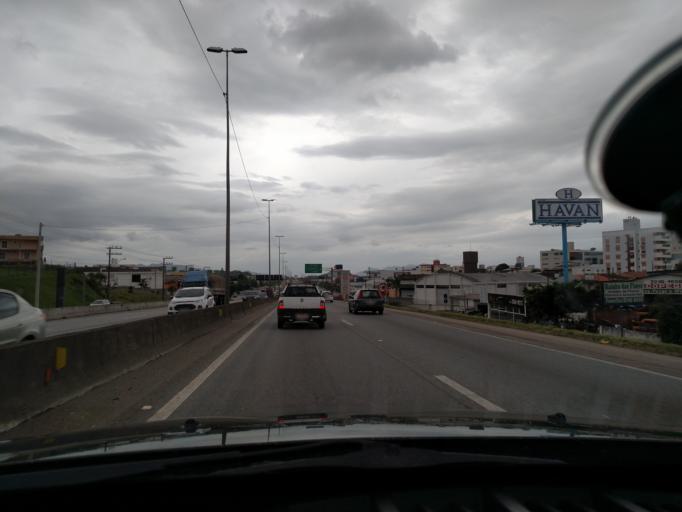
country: BR
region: Santa Catarina
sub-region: Sao Jose
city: Campinas
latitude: -27.5724
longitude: -48.6136
